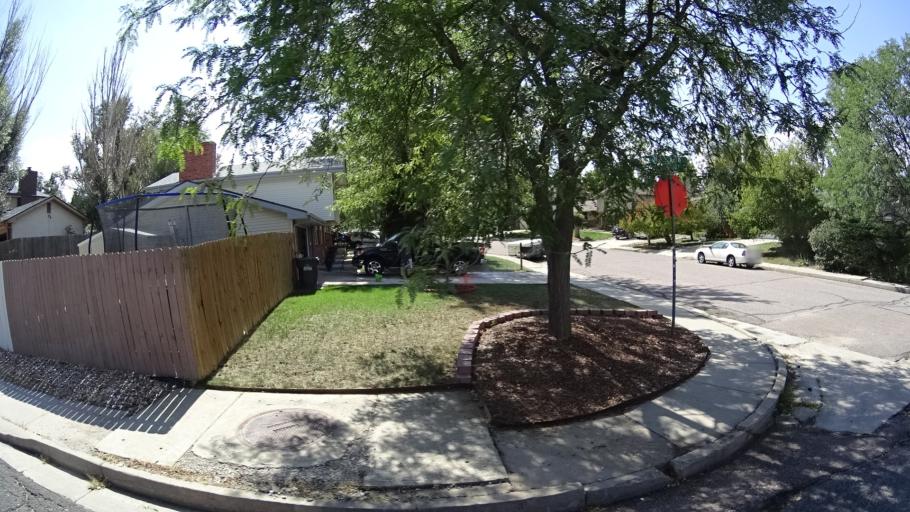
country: US
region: Colorado
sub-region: El Paso County
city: Cimarron Hills
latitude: 38.8730
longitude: -104.7380
